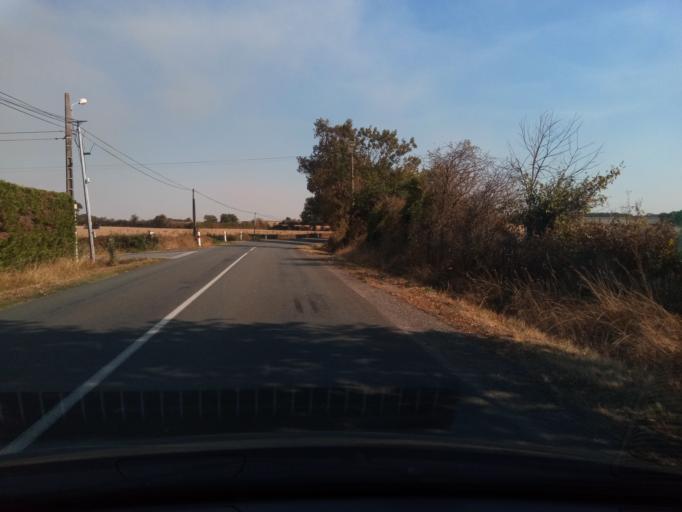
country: FR
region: Poitou-Charentes
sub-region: Departement de la Vienne
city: Montmorillon
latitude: 46.4442
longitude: 0.8306
